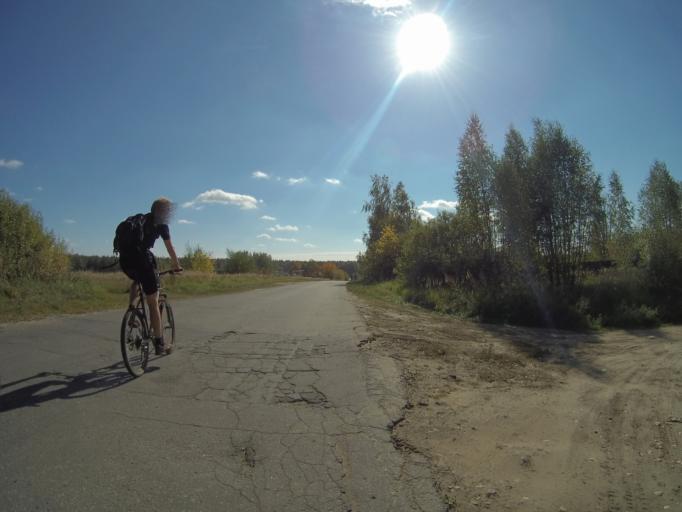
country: RU
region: Vladimir
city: Raduzhnyy
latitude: 55.9636
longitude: 40.2486
